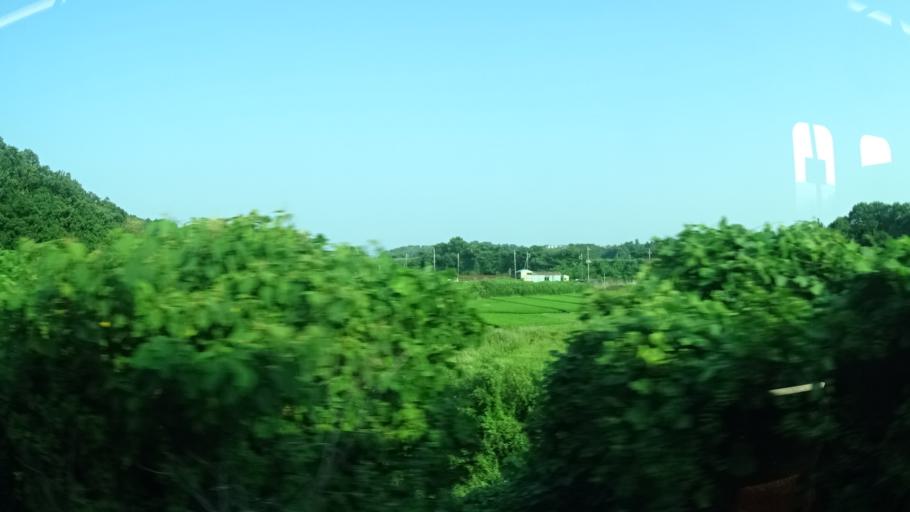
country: JP
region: Ibaraki
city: Hitachi
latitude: 36.6515
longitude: 140.6797
